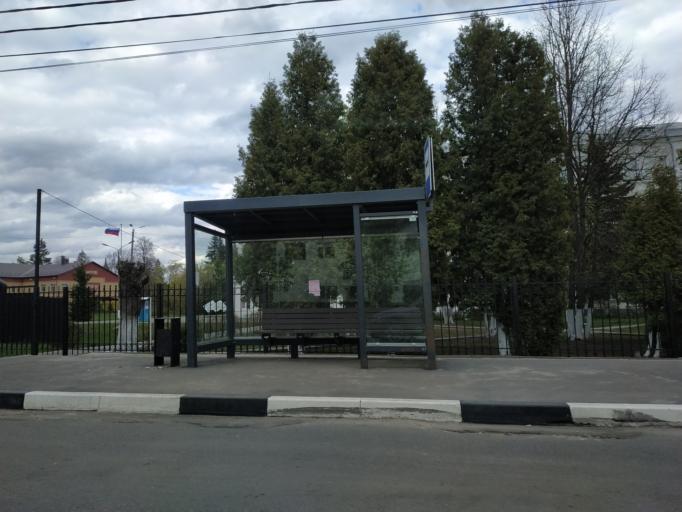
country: RU
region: Moskovskaya
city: Pavlovskiy Posad
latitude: 55.7850
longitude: 38.6487
